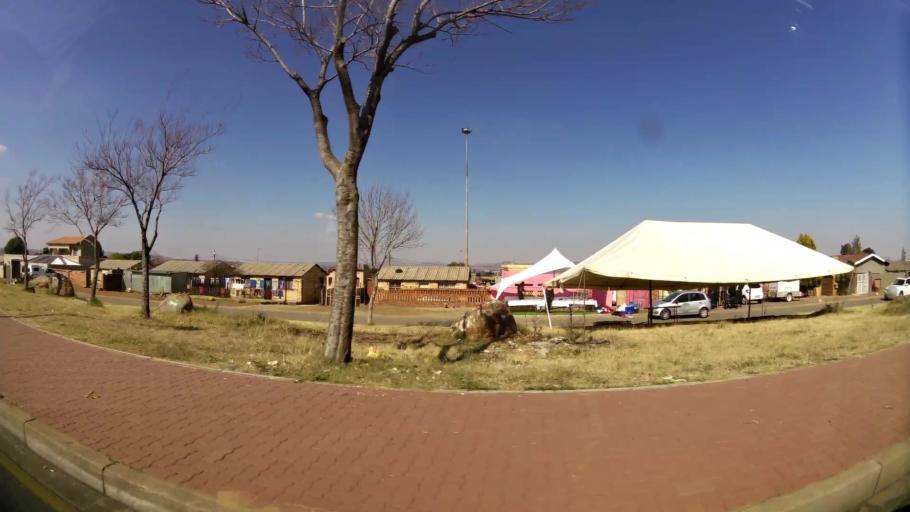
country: ZA
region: Gauteng
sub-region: City of Johannesburg Metropolitan Municipality
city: Soweto
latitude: -26.2755
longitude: 27.8694
